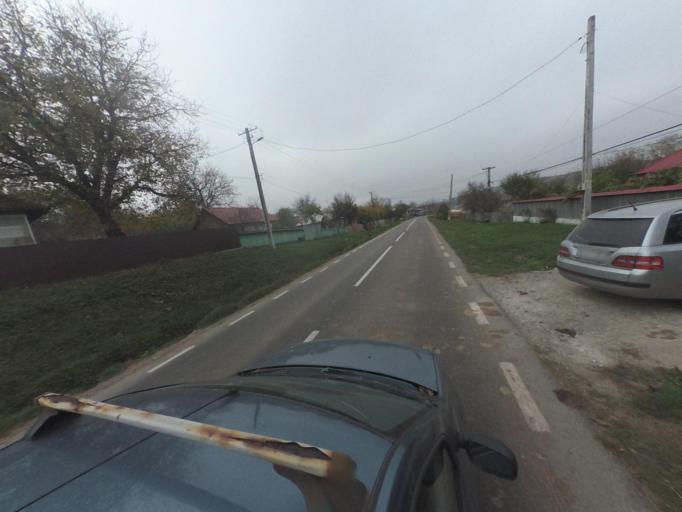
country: RO
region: Vaslui
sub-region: Comuna Bacesti
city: Bacesti
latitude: 46.8345
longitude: 27.2310
